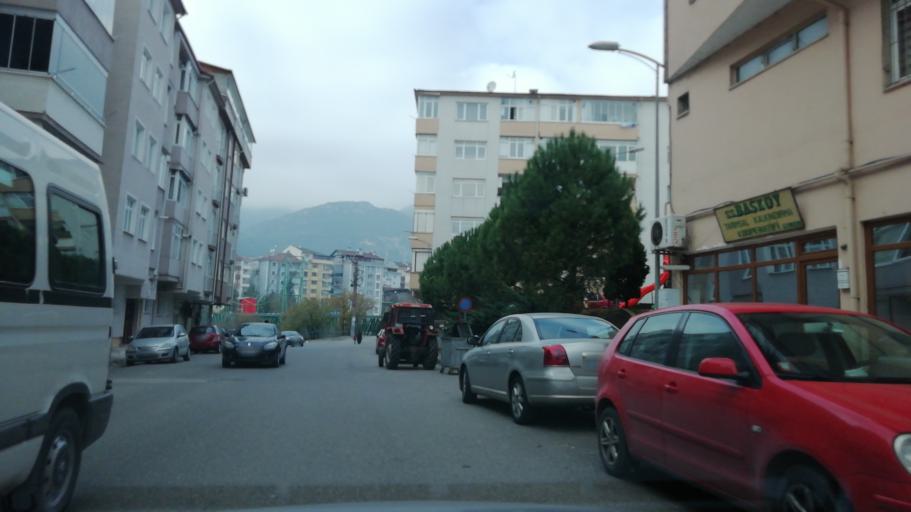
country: TR
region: Karabuk
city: Karabuk
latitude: 41.2066
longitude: 32.6263
